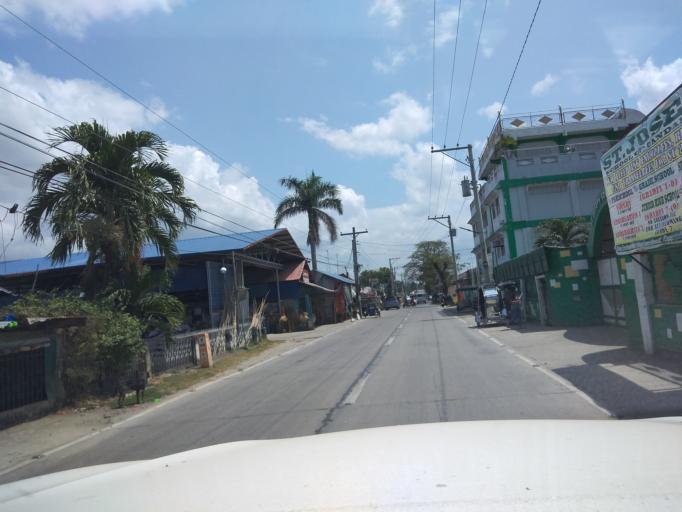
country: PH
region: Central Luzon
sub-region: Province of Pampanga
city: Lourdes
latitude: 15.0193
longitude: 120.8606
